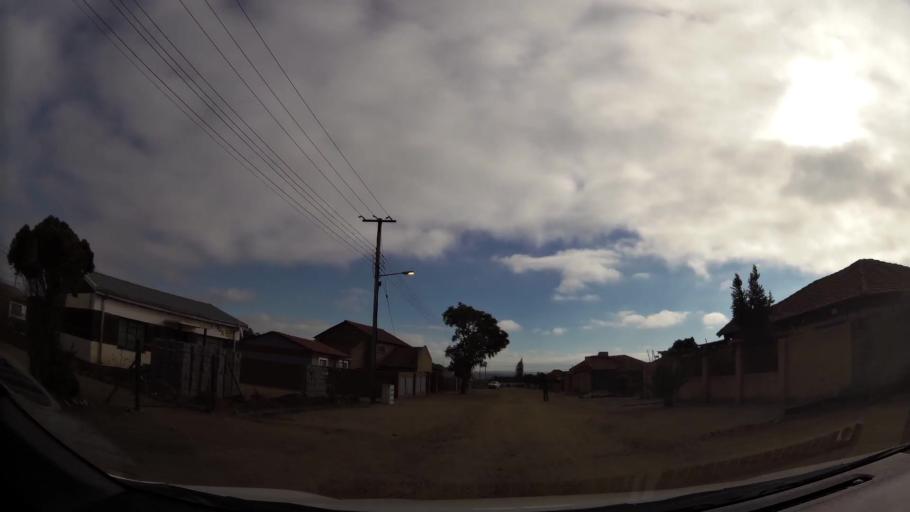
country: ZA
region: Limpopo
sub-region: Capricorn District Municipality
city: Polokwane
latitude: -23.8449
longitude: 29.3799
